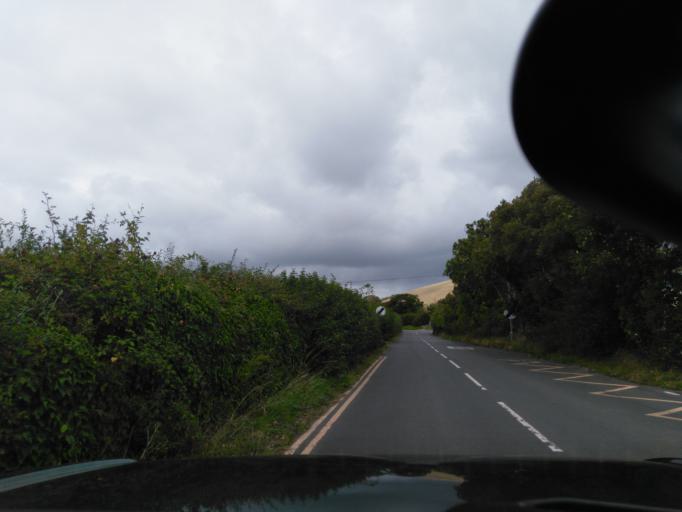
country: GB
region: England
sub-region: Dorset
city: Swanage
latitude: 50.6213
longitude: -1.9660
